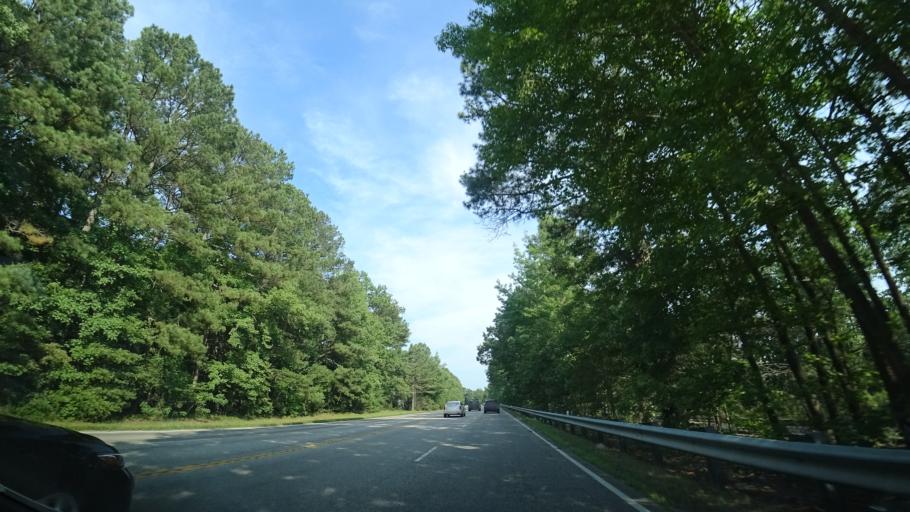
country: US
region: Virginia
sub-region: York County
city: Yorktown
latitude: 37.2186
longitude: -76.6083
